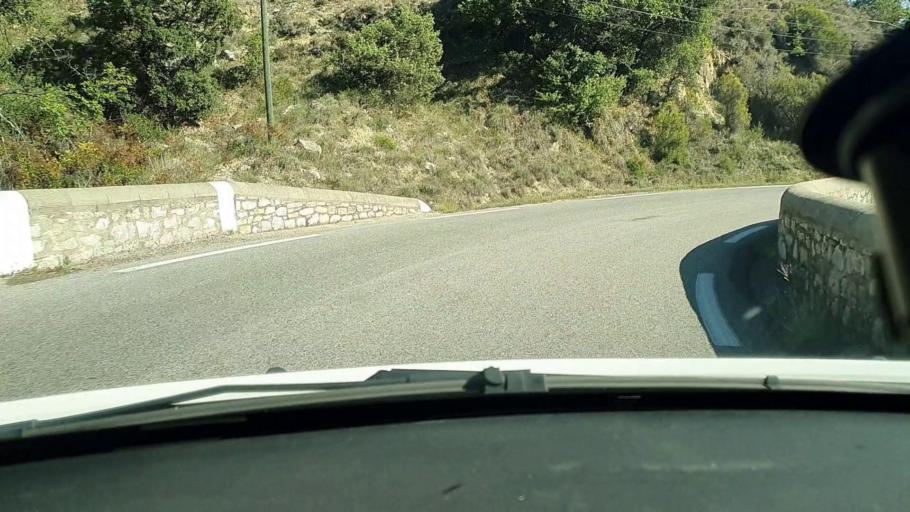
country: FR
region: Languedoc-Roussillon
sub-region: Departement du Gard
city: Saint-Julien-de-Peyrolas
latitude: 44.2939
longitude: 4.4859
